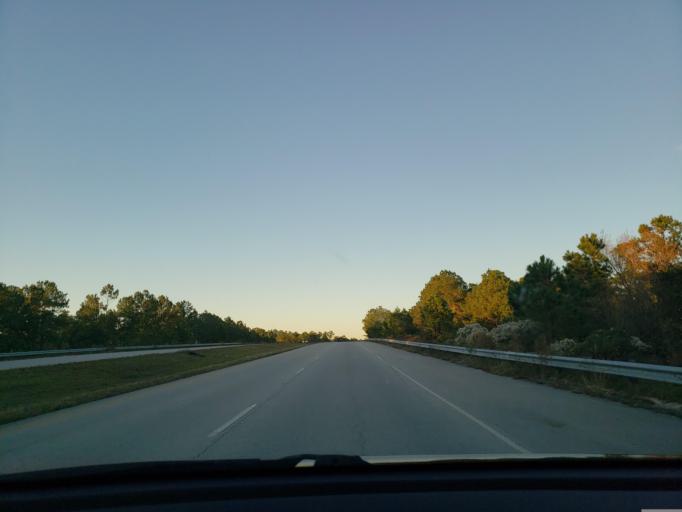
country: US
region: North Carolina
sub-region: Onslow County
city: Sneads Ferry
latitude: 34.6119
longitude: -77.4835
